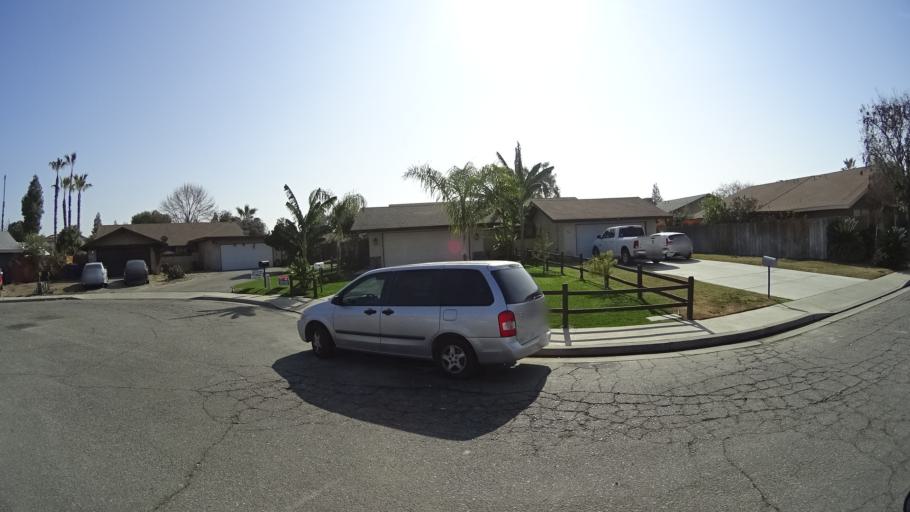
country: US
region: California
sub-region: Kern County
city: Bakersfield
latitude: 35.3344
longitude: -119.0666
